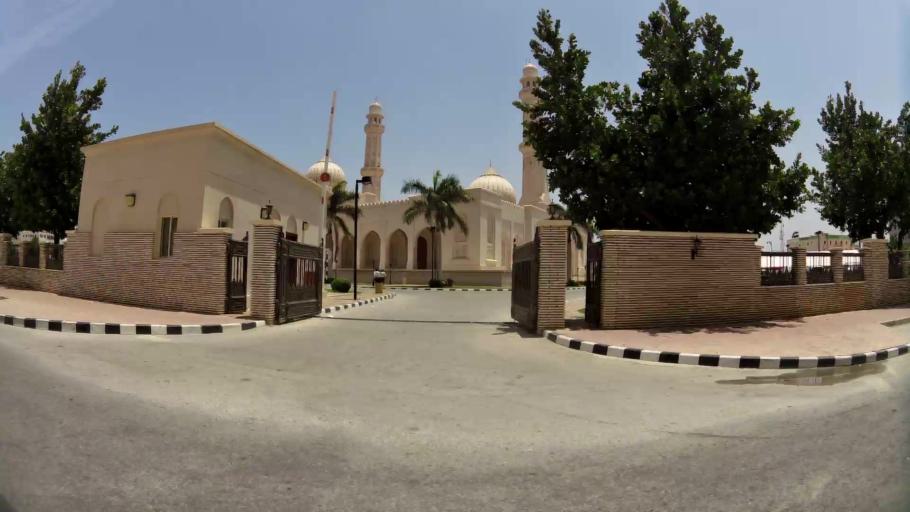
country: OM
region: Zufar
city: Salalah
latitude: 17.0176
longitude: 54.0949
